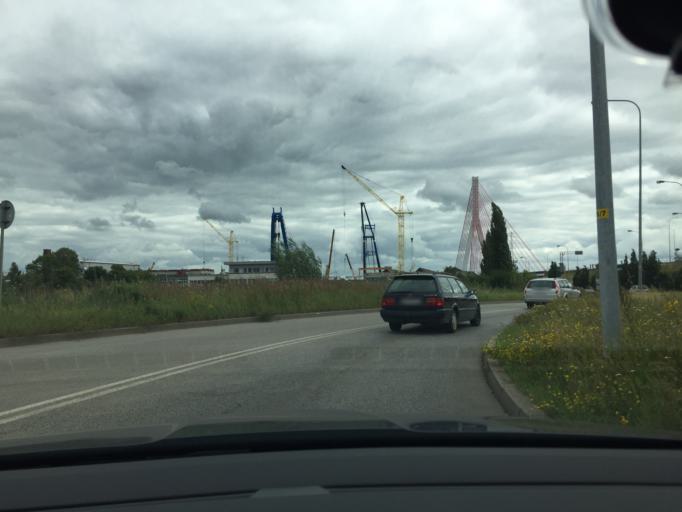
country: PL
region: Pomeranian Voivodeship
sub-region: Gdansk
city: Gdansk
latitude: 54.3600
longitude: 18.6931
